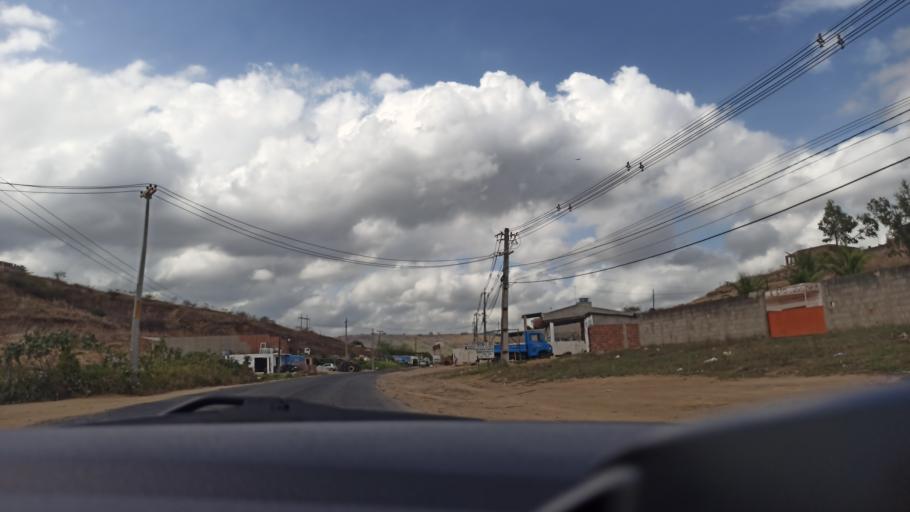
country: BR
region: Pernambuco
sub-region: Timbauba
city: Timbauba
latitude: -7.5035
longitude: -35.2991
